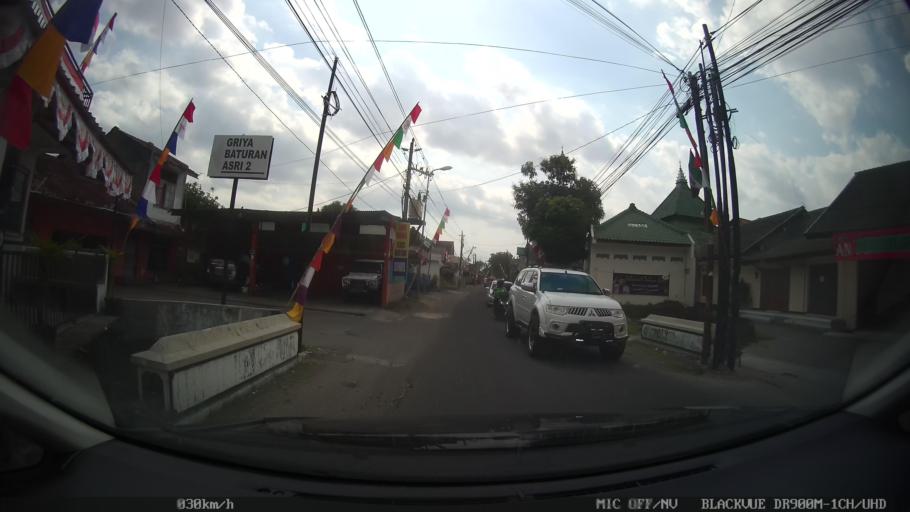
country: ID
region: Daerah Istimewa Yogyakarta
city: Yogyakarta
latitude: -7.7650
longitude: 110.3498
